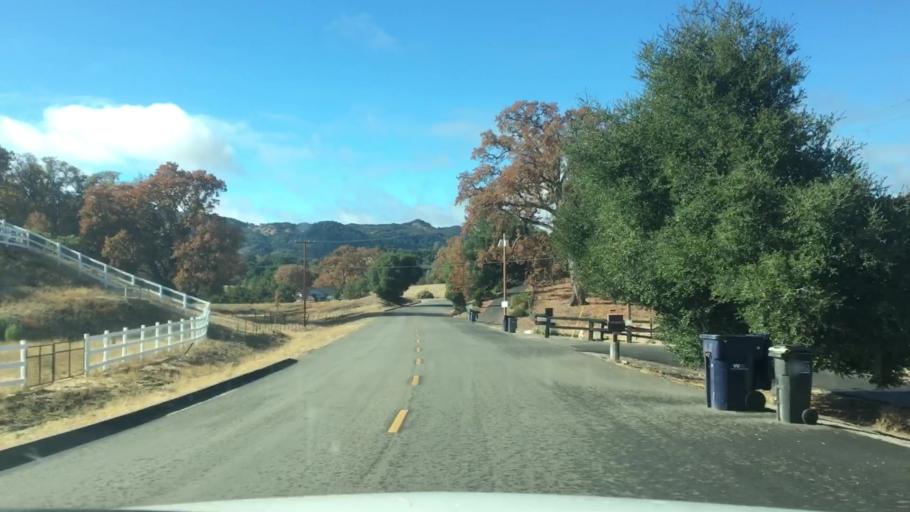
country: US
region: California
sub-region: San Luis Obispo County
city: Atascadero
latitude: 35.4427
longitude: -120.6401
